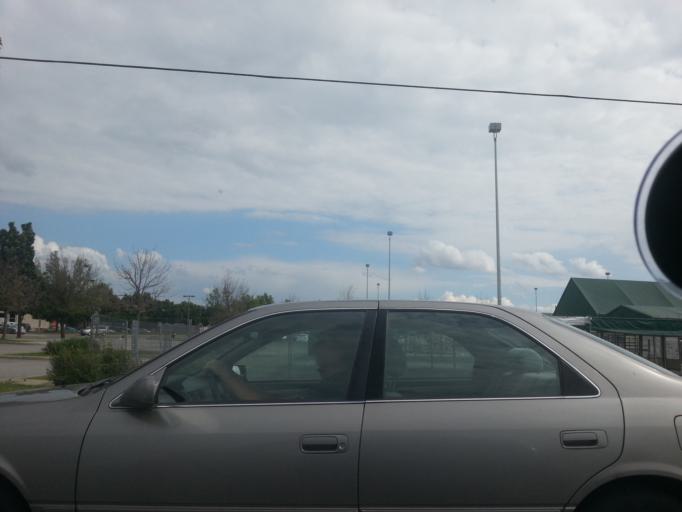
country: CA
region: Quebec
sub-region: Outaouais
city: Gatineau
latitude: 45.4812
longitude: -75.6815
